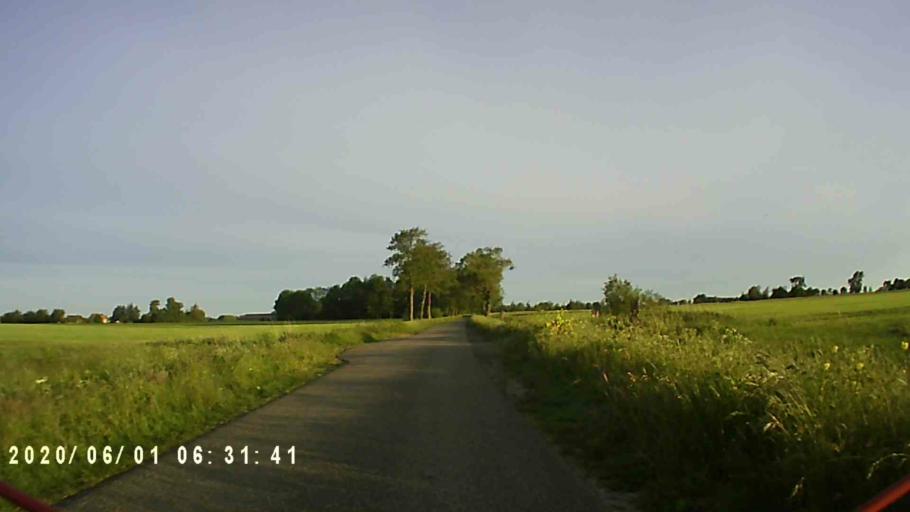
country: NL
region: Friesland
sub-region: Gemeente Kollumerland en Nieuwkruisland
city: Kollum
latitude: 53.2728
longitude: 6.1790
